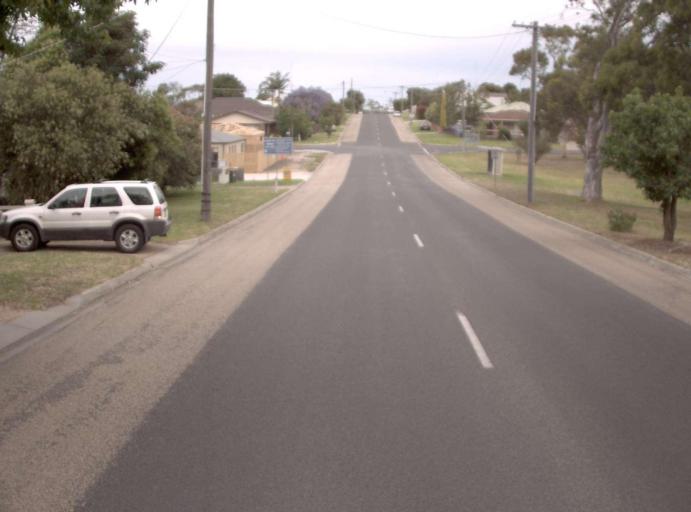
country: AU
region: Victoria
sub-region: East Gippsland
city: Bairnsdale
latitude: -37.9141
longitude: 147.7193
